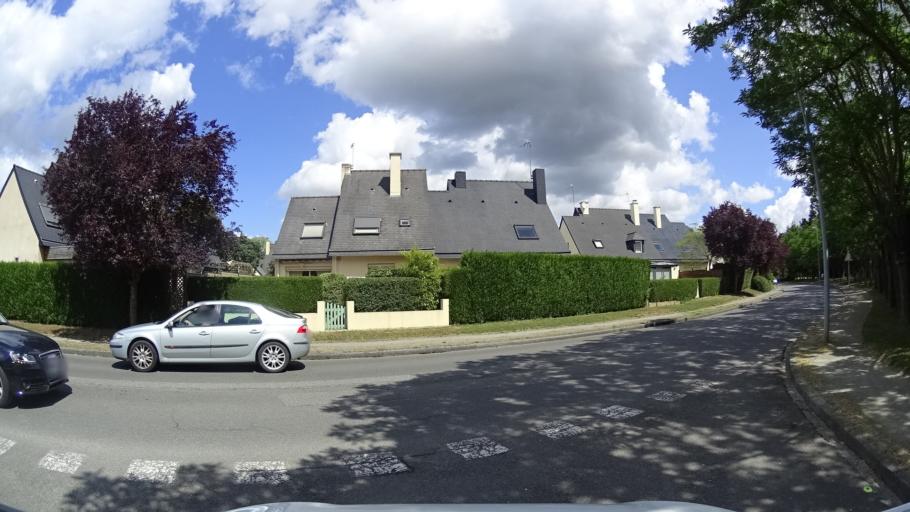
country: FR
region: Brittany
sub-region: Departement d'Ille-et-Vilaine
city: Chartres-de-Bretagne
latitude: 48.0317
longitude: -1.7081
